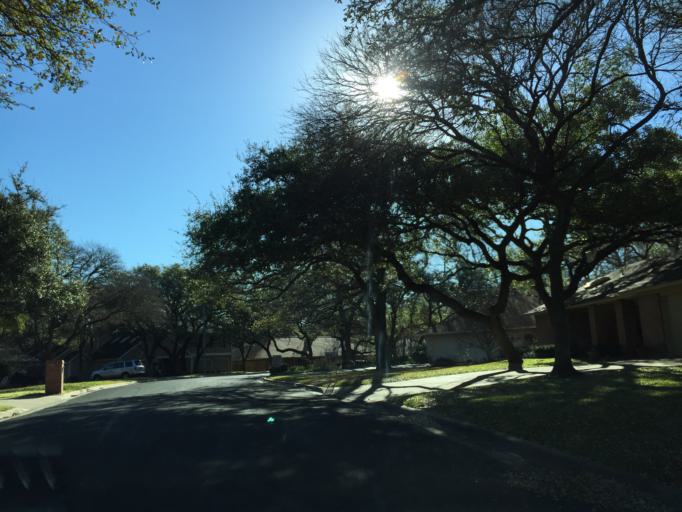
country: US
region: Texas
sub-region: Williamson County
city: Jollyville
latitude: 30.4069
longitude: -97.7379
